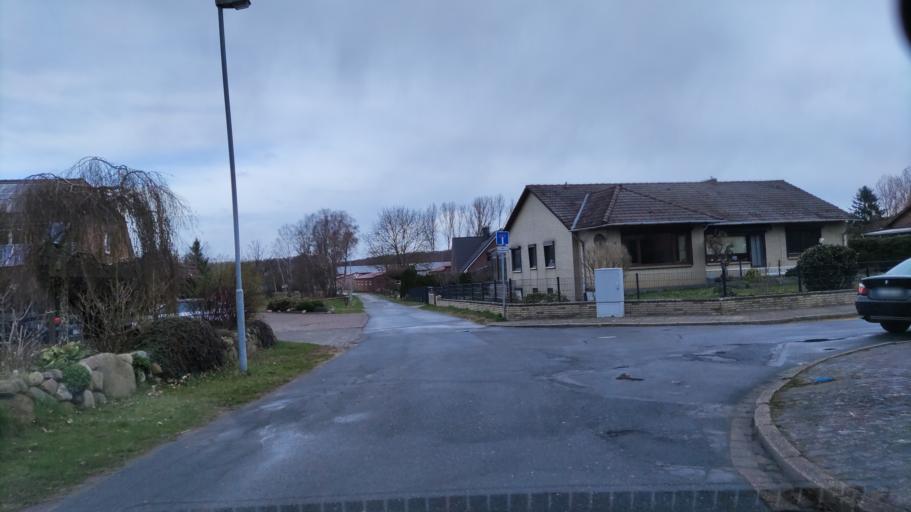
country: DE
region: Lower Saxony
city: Dahlenburg
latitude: 53.1929
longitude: 10.7262
